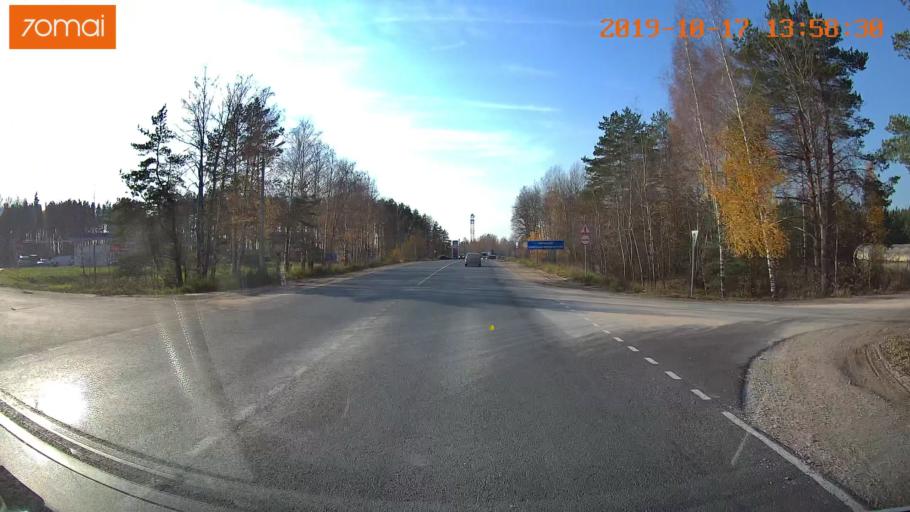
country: RU
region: Rjazan
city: Spas-Klepiki
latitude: 55.1394
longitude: 40.2223
